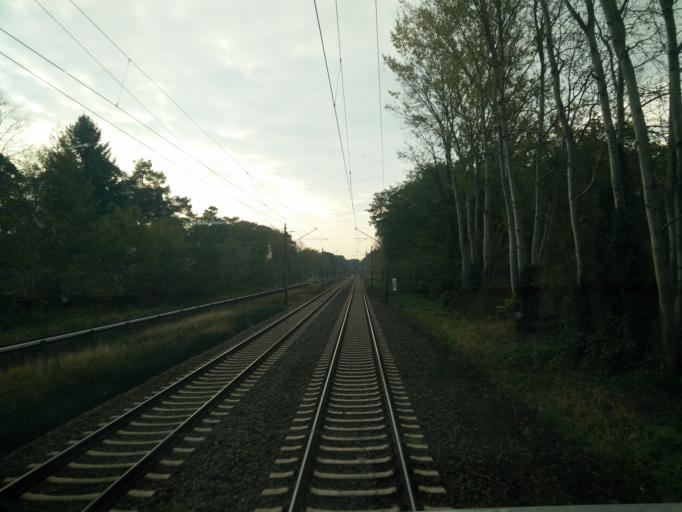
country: DE
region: Brandenburg
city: Wildau
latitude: 52.3408
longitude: 13.6325
